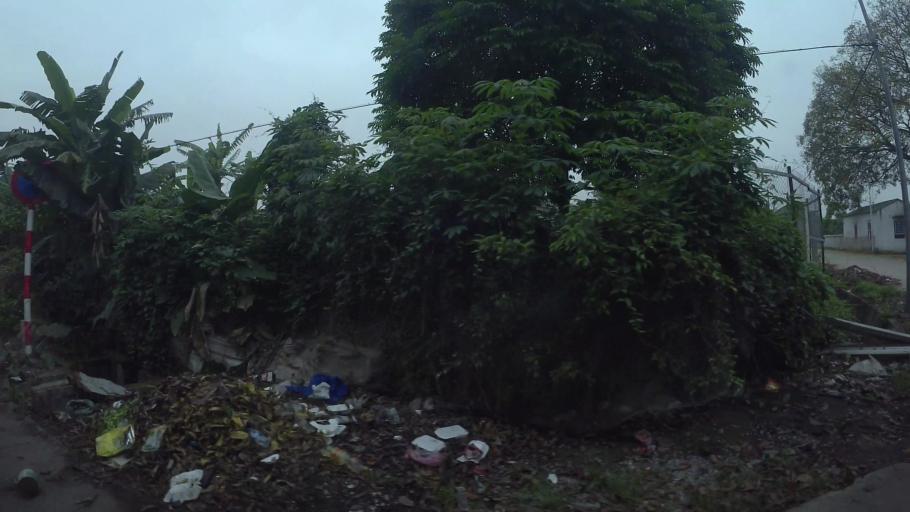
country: VN
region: Hung Yen
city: Van Giang
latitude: 20.9756
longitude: 105.8907
